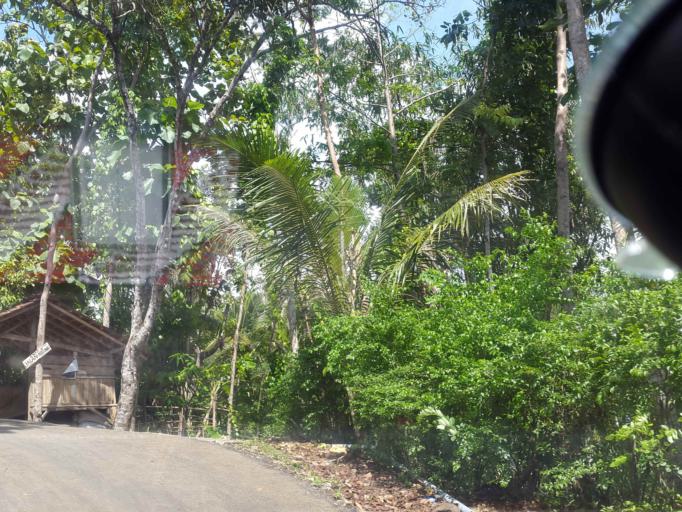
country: ID
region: East Java
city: Sumberdadi
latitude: -8.0068
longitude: 111.6903
